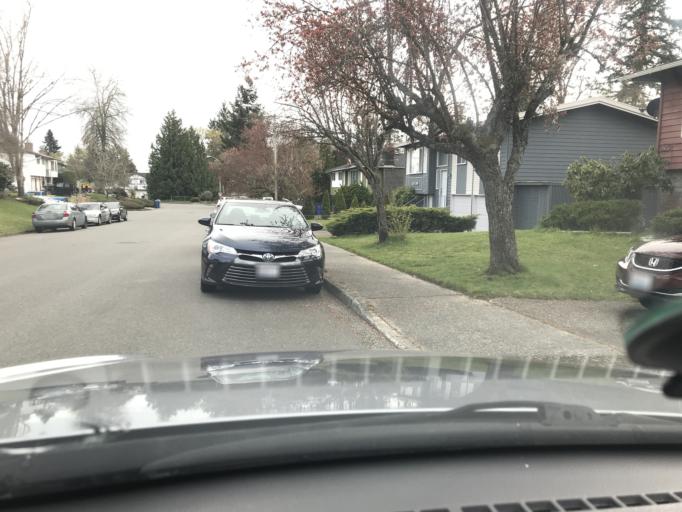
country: US
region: Washington
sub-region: King County
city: East Hill-Meridian
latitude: 47.4124
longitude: -122.1753
